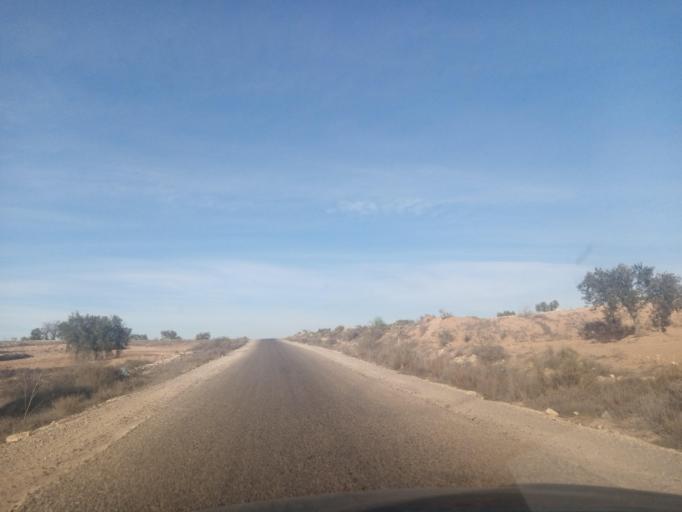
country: TN
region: Safaqis
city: Bi'r `Ali Bin Khalifah
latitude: 34.8457
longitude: 10.1595
